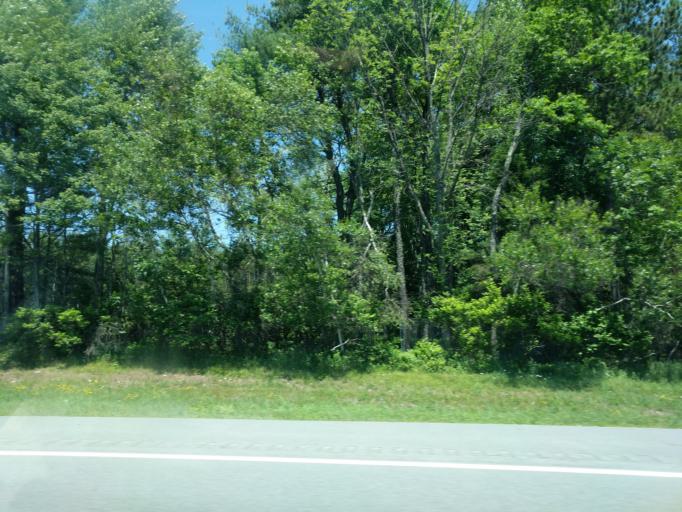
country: US
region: New York
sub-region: Sullivan County
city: Monticello
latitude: 41.6468
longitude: -74.6522
